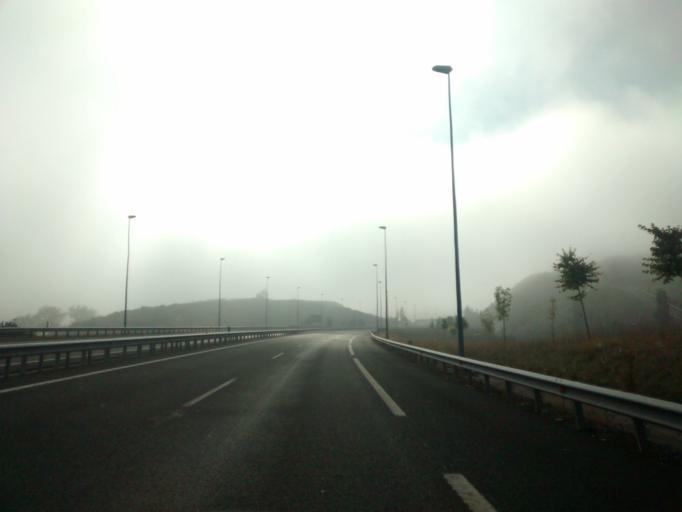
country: ES
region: Cantabria
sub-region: Provincia de Cantabria
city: Arenas de Iguna
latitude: 43.1858
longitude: -4.0615
